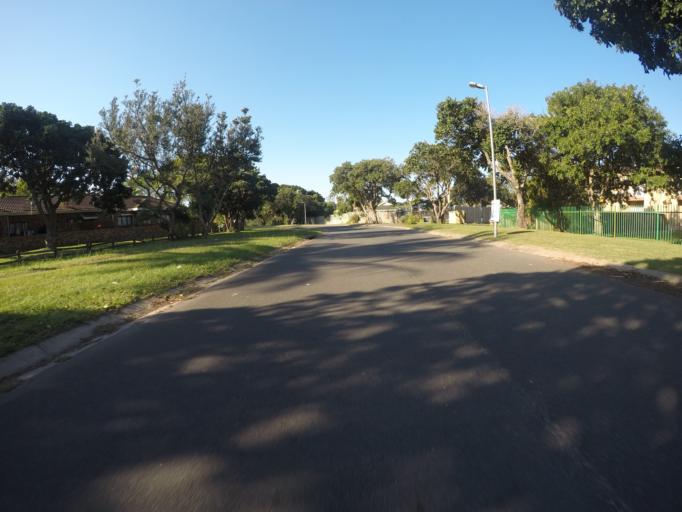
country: ZA
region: KwaZulu-Natal
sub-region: uThungulu District Municipality
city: Richards Bay
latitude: -28.7885
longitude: 32.1017
